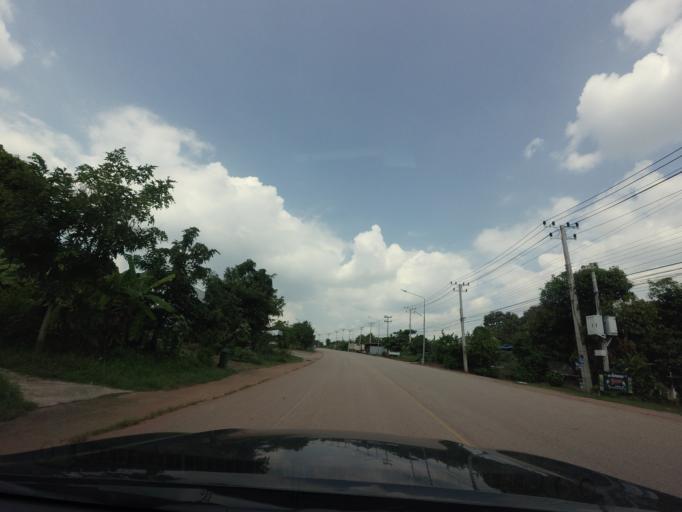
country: TH
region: Uttaradit
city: Ban Khok
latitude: 18.0216
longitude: 101.0711
